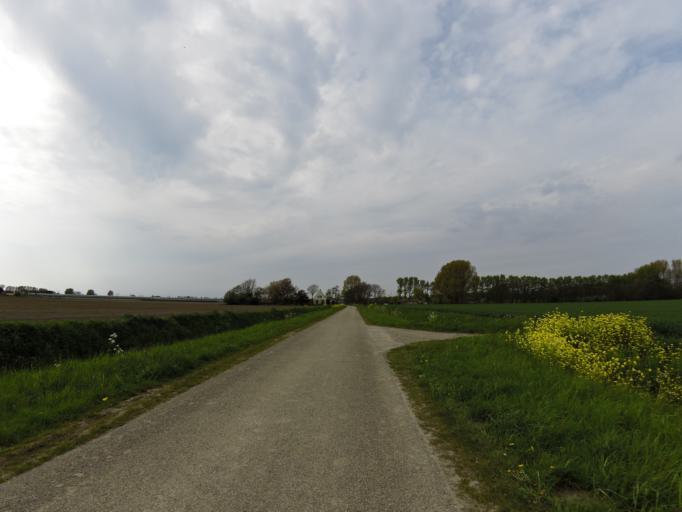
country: NL
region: South Holland
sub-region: Gemeente Brielle
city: Brielle
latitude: 51.9143
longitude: 4.1624
